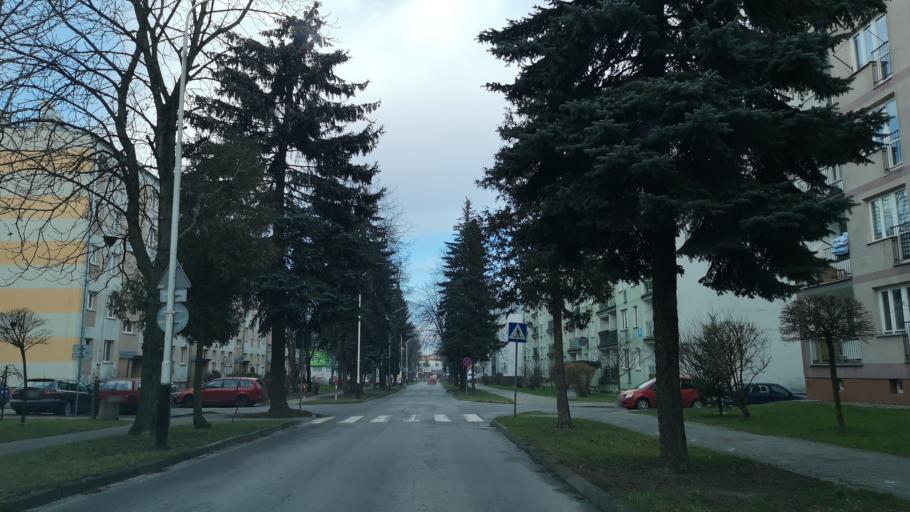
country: PL
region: Subcarpathian Voivodeship
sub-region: Powiat lezajski
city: Lezajsk
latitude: 50.2595
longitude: 22.4175
